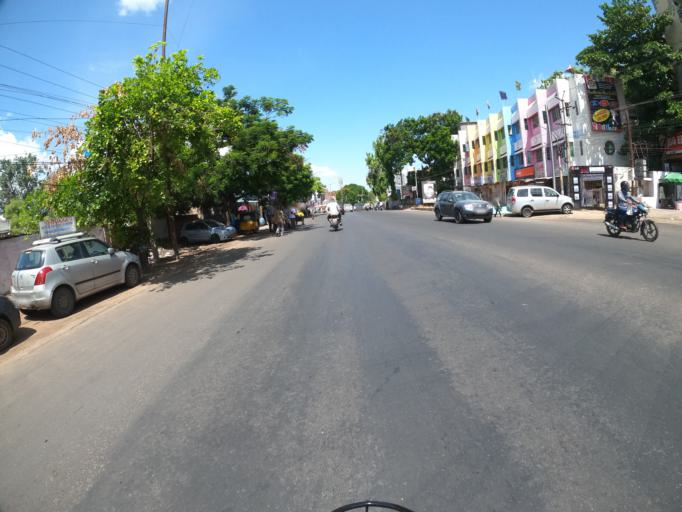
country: IN
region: Telangana
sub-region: Hyderabad
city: Hyderabad
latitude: 17.3735
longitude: 78.4161
